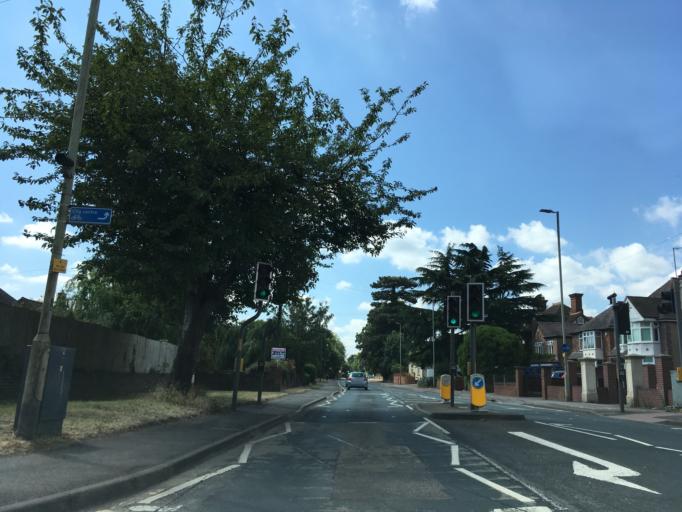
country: GB
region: England
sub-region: Gloucestershire
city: Gloucester
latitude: 51.8806
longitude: -2.2395
